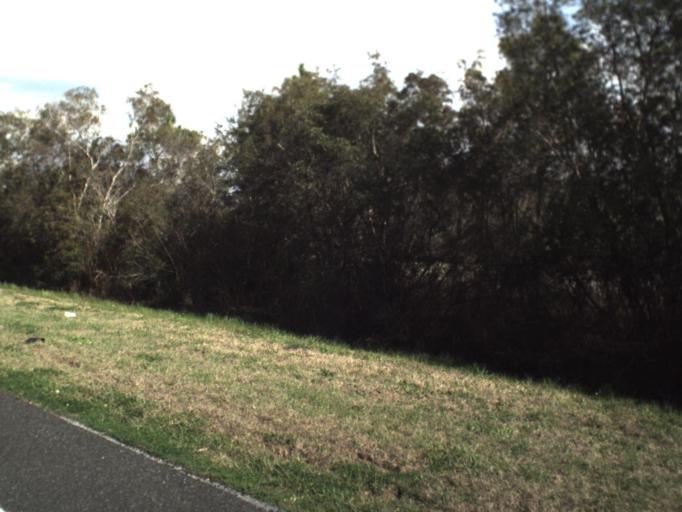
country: US
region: Florida
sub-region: Bay County
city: Youngstown
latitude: 30.2840
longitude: -85.5073
